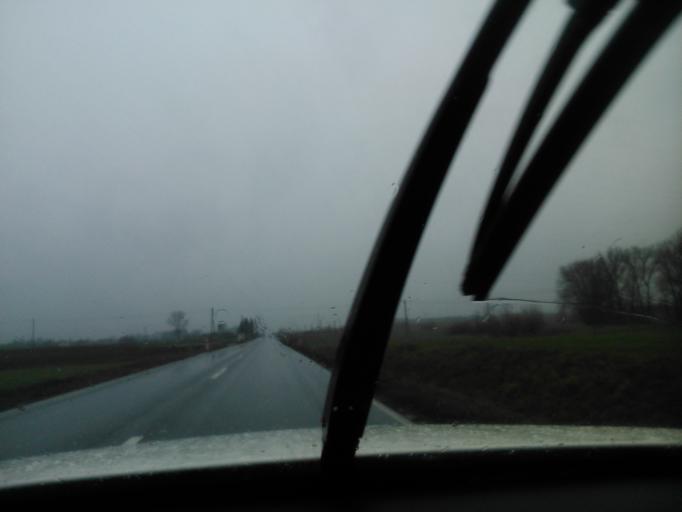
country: PL
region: Kujawsko-Pomorskie
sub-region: Powiat golubsko-dobrzynski
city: Radomin
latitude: 53.0792
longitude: 19.2282
